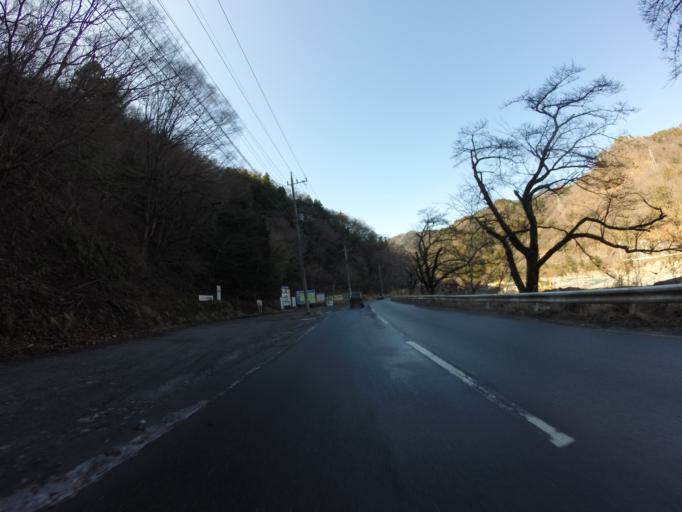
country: JP
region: Yamanashi
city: Ryuo
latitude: 35.4220
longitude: 138.4044
